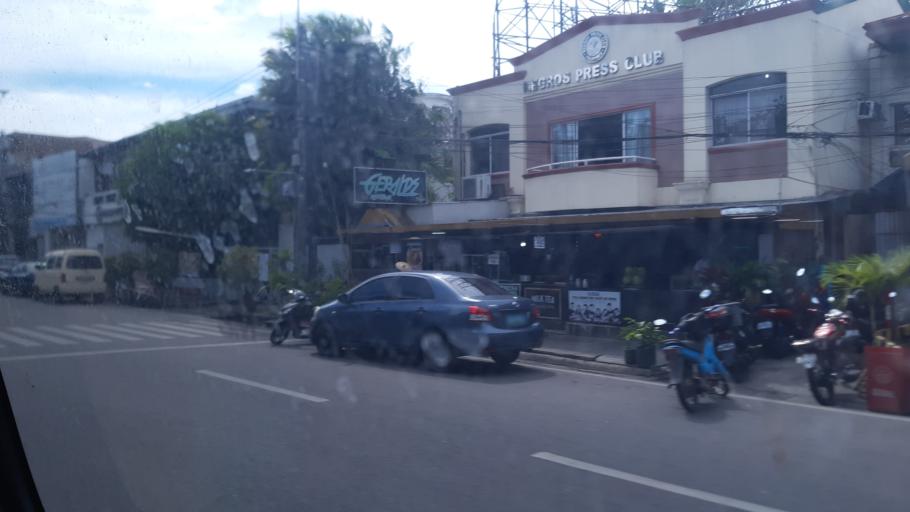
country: PH
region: Western Visayas
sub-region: Province of Negros Occidental
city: Bacolod City
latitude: 10.6695
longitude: 122.9455
